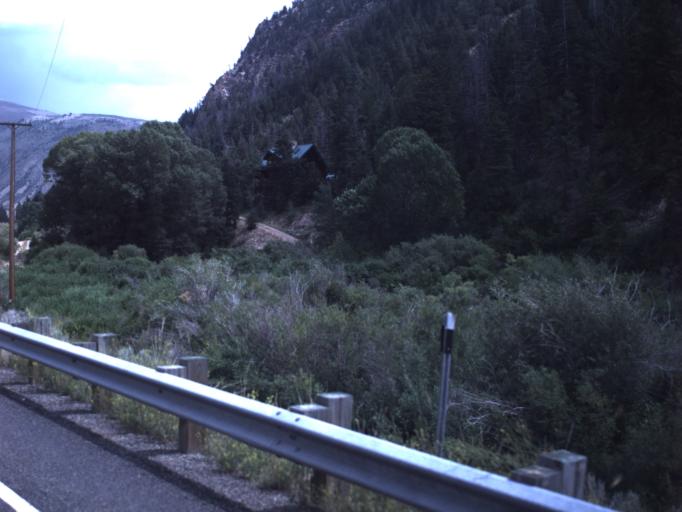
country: US
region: Utah
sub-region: Summit County
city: Francis
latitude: 40.4574
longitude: -110.8509
